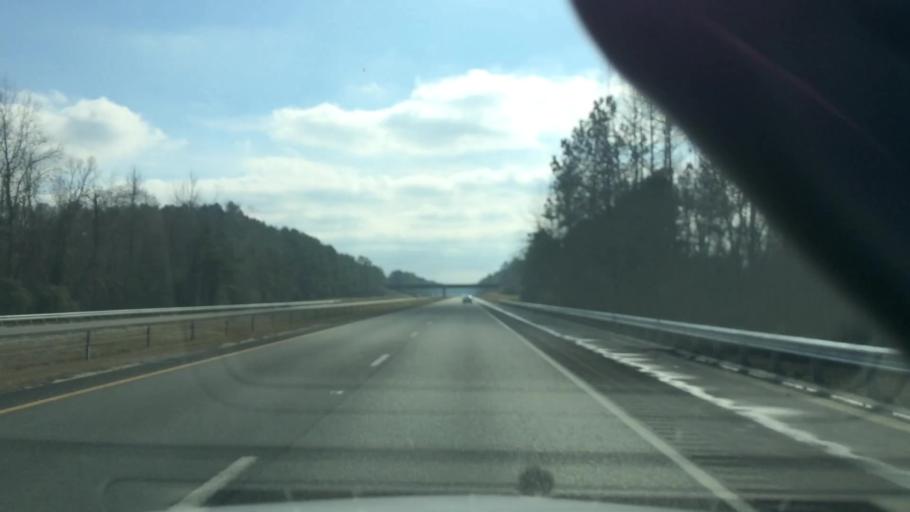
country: US
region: North Carolina
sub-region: Pender County
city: Rocky Point
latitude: 34.4837
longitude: -77.8785
